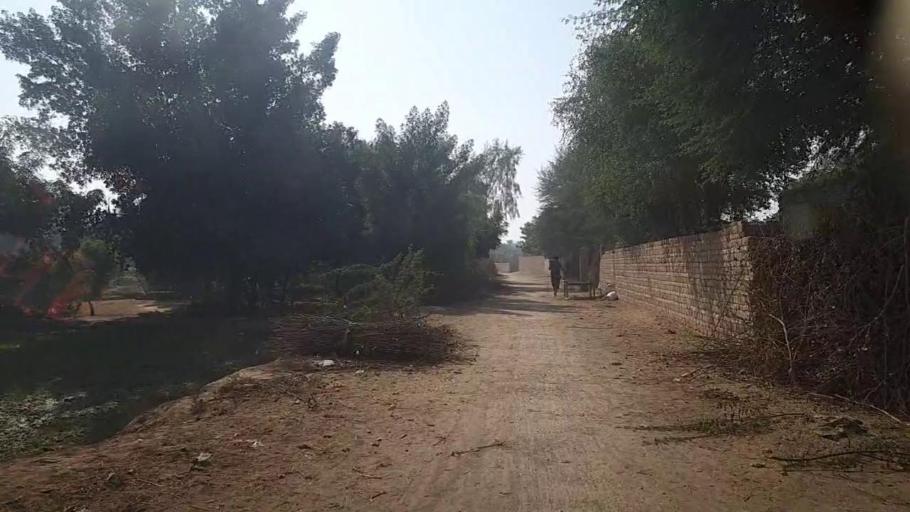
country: PK
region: Sindh
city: Kandiari
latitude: 27.0228
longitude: 68.5079
